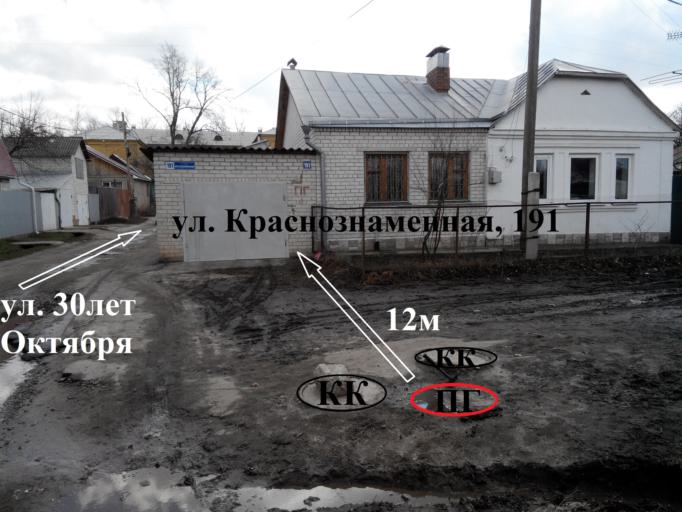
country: RU
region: Voronezj
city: Voronezh
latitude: 51.6338
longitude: 39.1696
